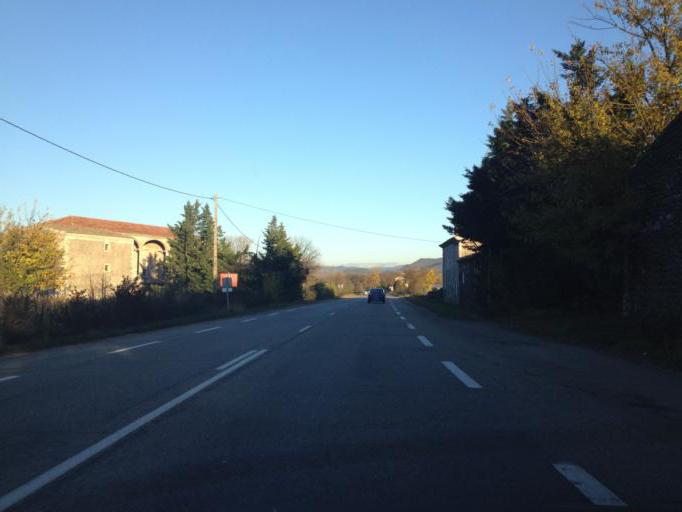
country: FR
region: Rhone-Alpes
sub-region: Departement de l'Ardeche
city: Chomerac
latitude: 44.7091
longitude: 4.6753
